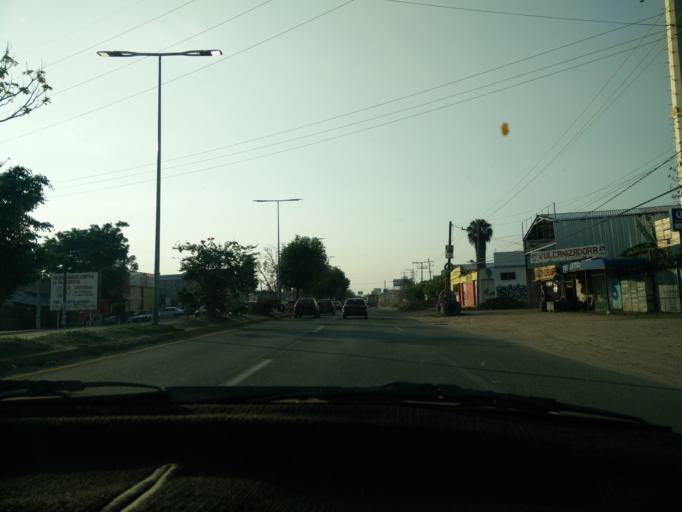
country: MX
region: Oaxaca
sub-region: Santa Maria Atzompa
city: Fraccionamiento Riberas de San Jeronimo
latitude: 17.1252
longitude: -96.7664
